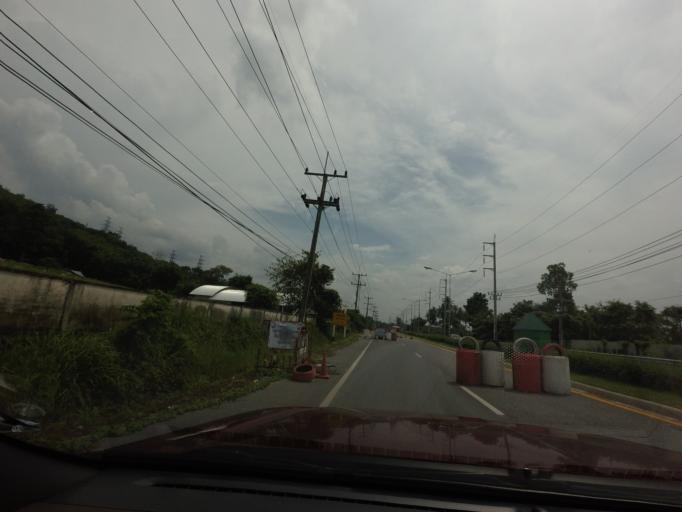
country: TH
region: Yala
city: Yala
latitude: 6.5013
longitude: 101.2720
